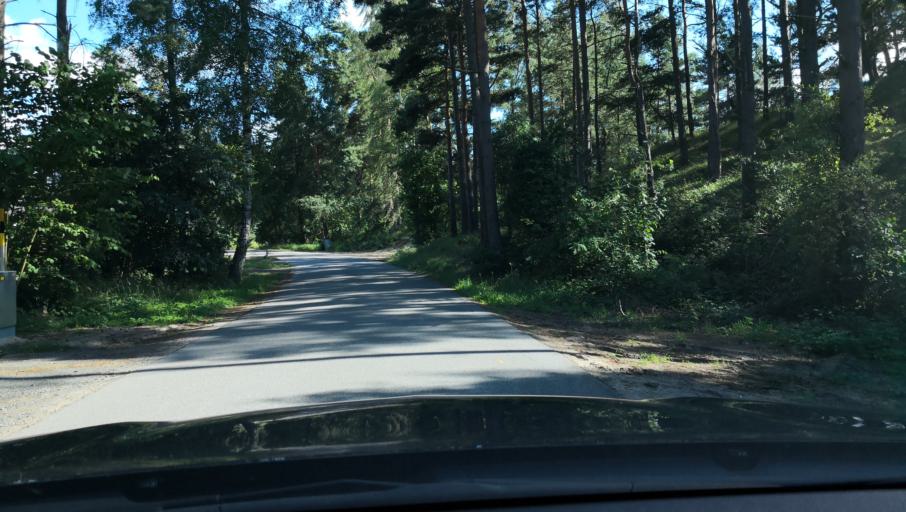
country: SE
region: Skane
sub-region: Simrishamns Kommun
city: Kivik
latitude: 55.7775
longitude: 14.1947
